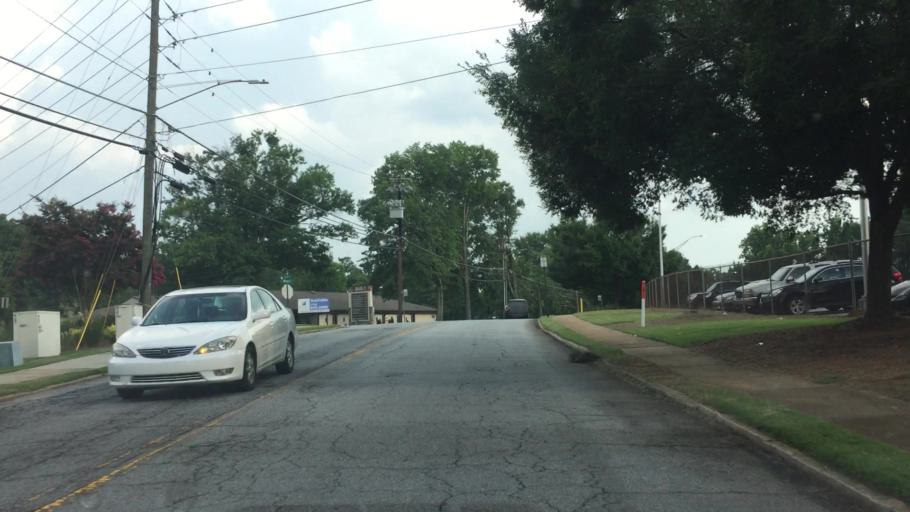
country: US
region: Georgia
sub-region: DeKalb County
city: Scottdale
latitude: 33.7894
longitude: -84.2797
